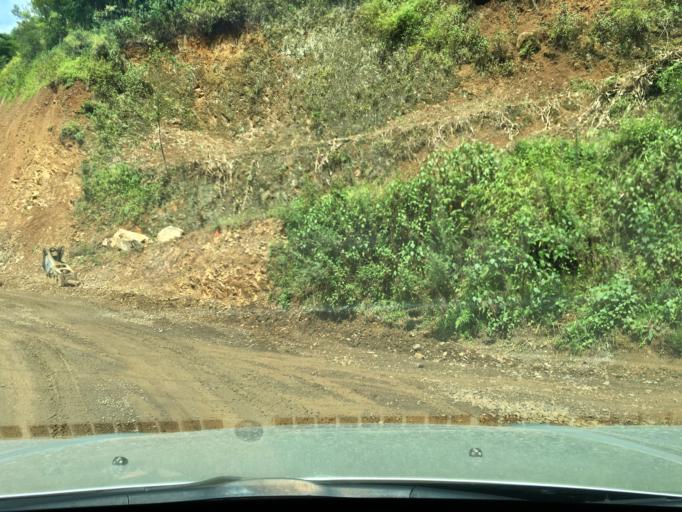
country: CN
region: Guizhou Sheng
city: Liupanshui
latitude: 25.9090
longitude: 105.1067
